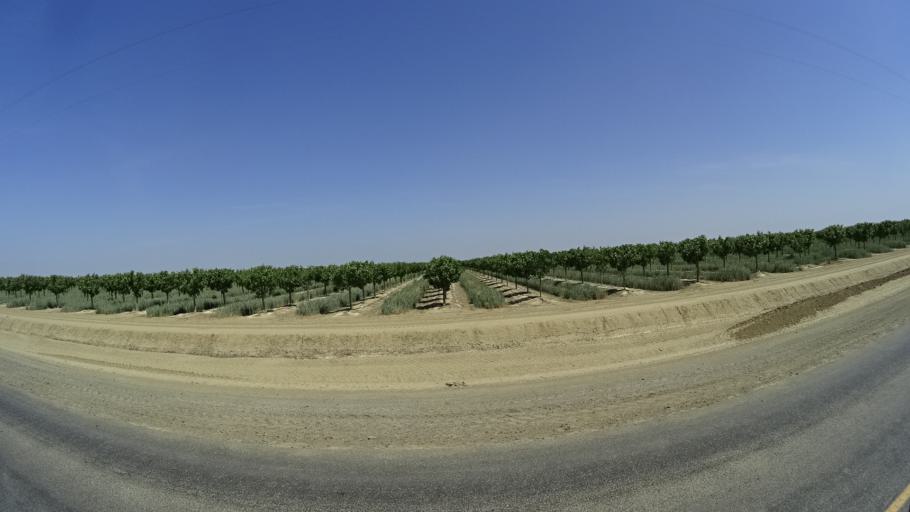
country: US
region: California
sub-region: Kings County
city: Kettleman City
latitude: 36.1377
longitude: -119.9544
